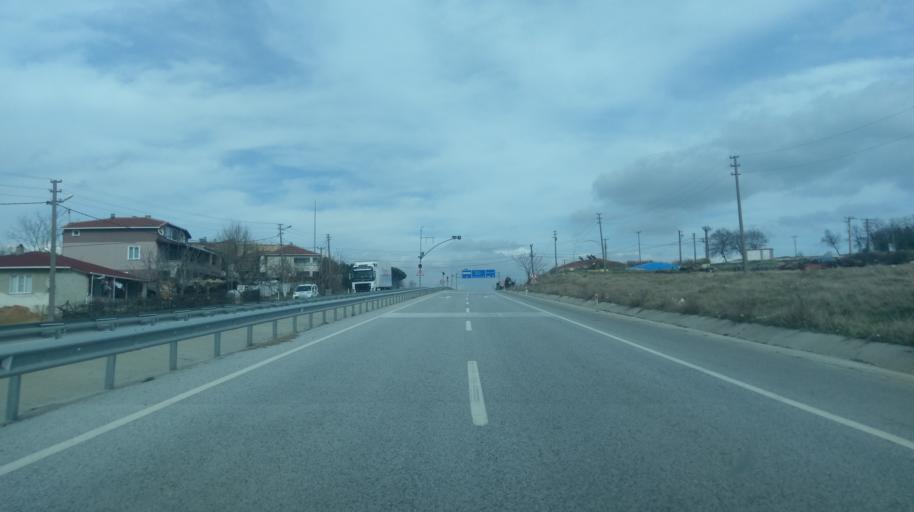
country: TR
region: Edirne
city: Kircasalih
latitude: 41.3892
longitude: 26.7985
